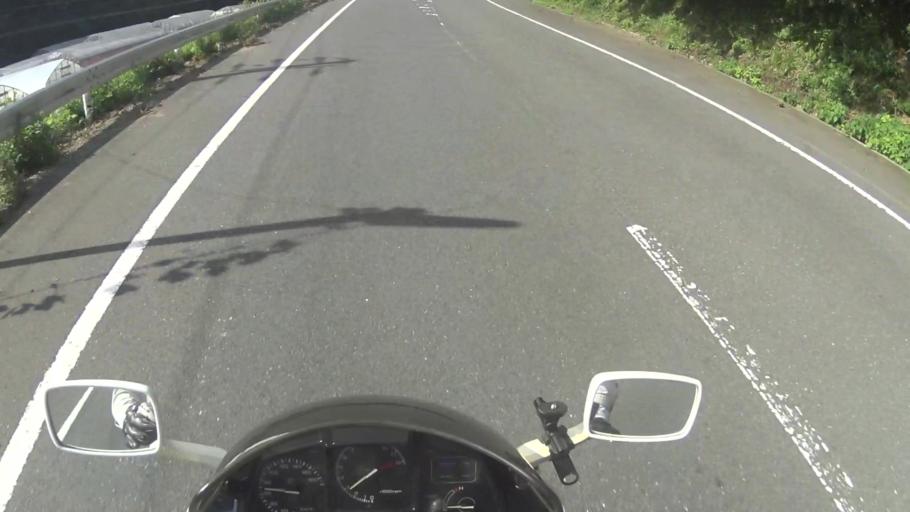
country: JP
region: Kyoto
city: Miyazu
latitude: 35.7343
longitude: 135.2561
